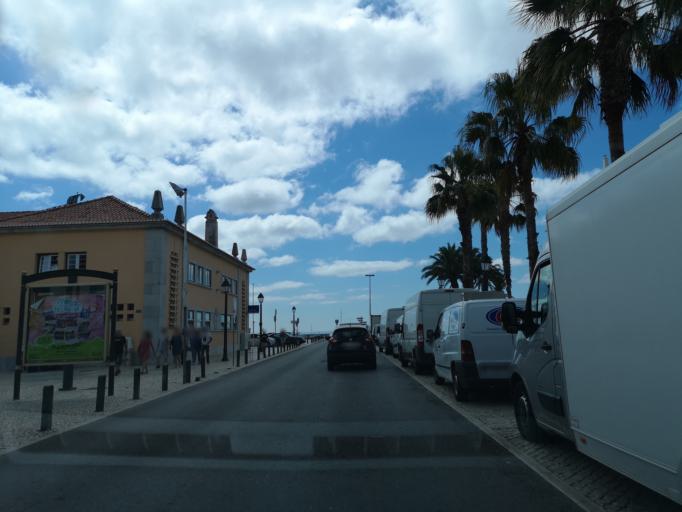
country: PT
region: Lisbon
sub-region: Cascais
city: Cascais
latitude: 38.6981
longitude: -9.4201
